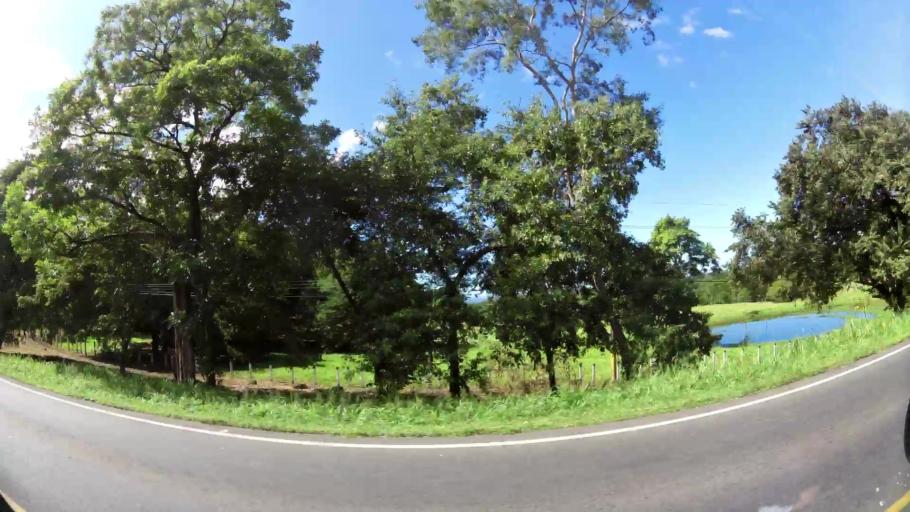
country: CR
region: Guanacaste
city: Juntas
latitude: 10.3167
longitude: -85.0450
